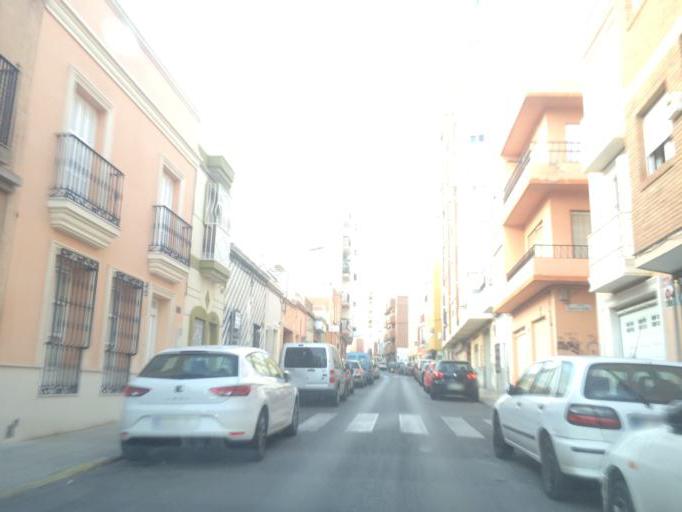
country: ES
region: Andalusia
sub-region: Provincia de Almeria
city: Almeria
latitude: 36.8446
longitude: -2.4658
